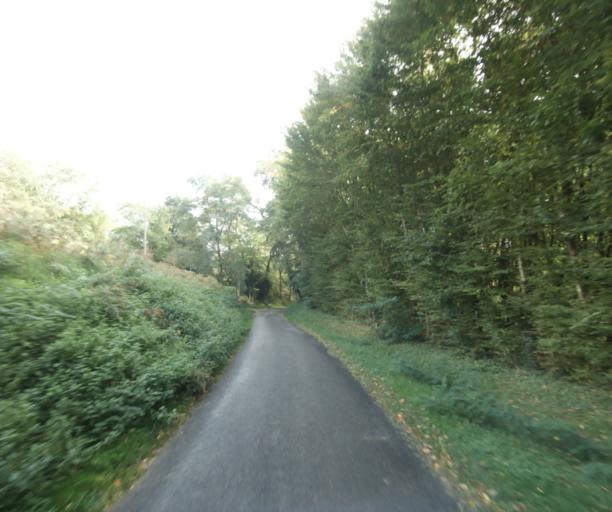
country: FR
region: Midi-Pyrenees
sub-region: Departement du Gers
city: Eauze
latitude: 43.8815
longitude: 0.1071
